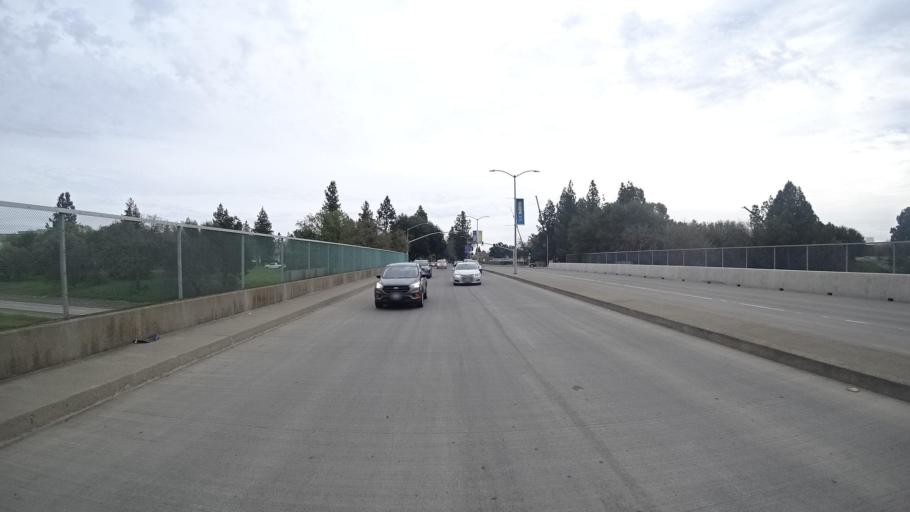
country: US
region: California
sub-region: Yolo County
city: Davis
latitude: 38.5459
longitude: -121.7683
